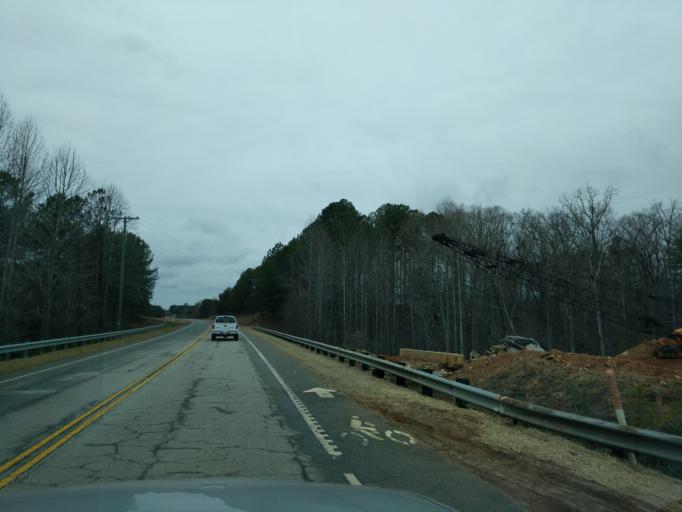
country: US
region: South Carolina
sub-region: Oconee County
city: Walhalla
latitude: 34.9134
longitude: -82.9358
